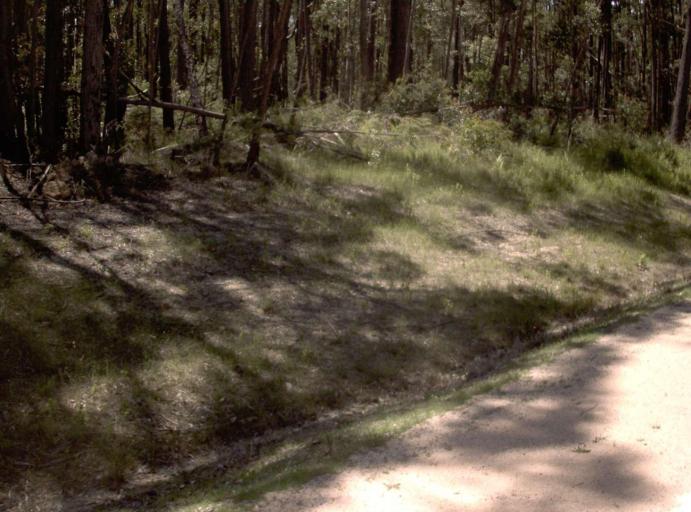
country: AU
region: Victoria
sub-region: East Gippsland
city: Lakes Entrance
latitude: -37.6754
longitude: 148.7895
